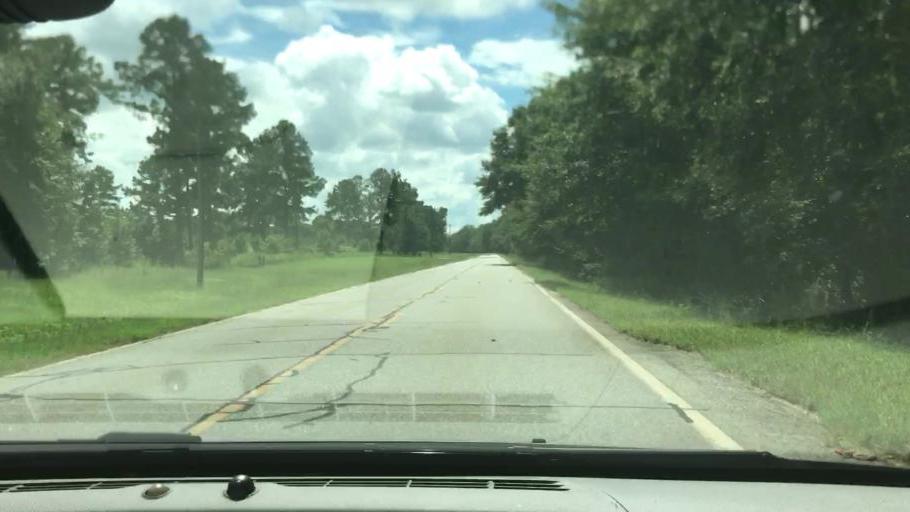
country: US
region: Georgia
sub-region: Quitman County
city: Georgetown
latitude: 32.1170
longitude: -85.0369
